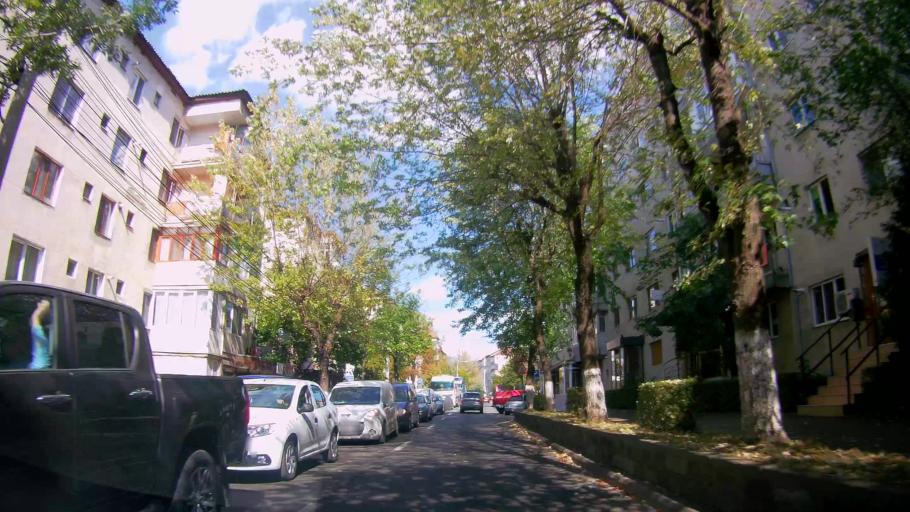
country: RO
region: Salaj
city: Zalau
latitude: 47.1870
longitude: 23.0597
